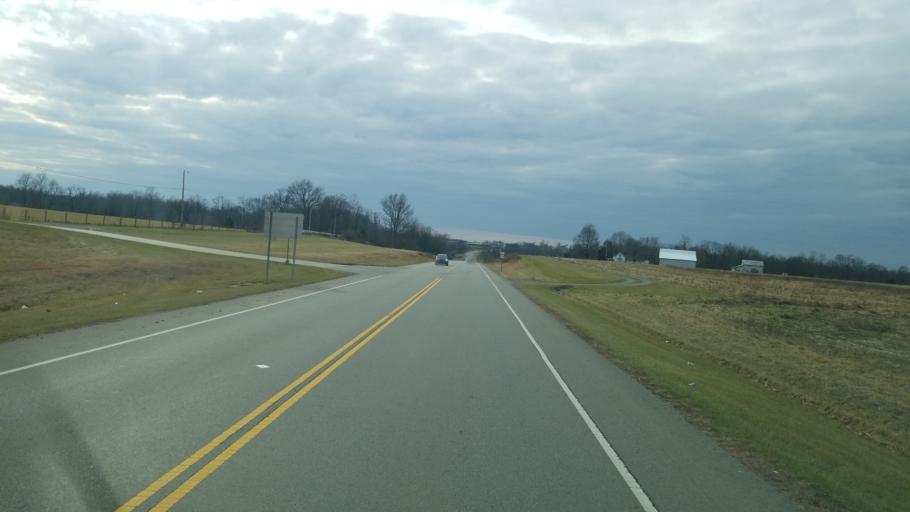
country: US
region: Ohio
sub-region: Highland County
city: Greenfield
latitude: 39.2274
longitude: -83.3891
